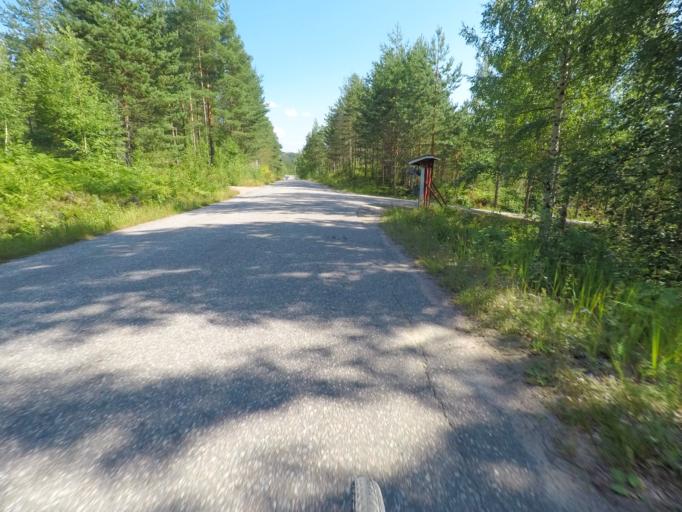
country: FI
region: Southern Savonia
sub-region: Mikkeli
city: Puumala
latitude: 61.4214
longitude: 28.1071
